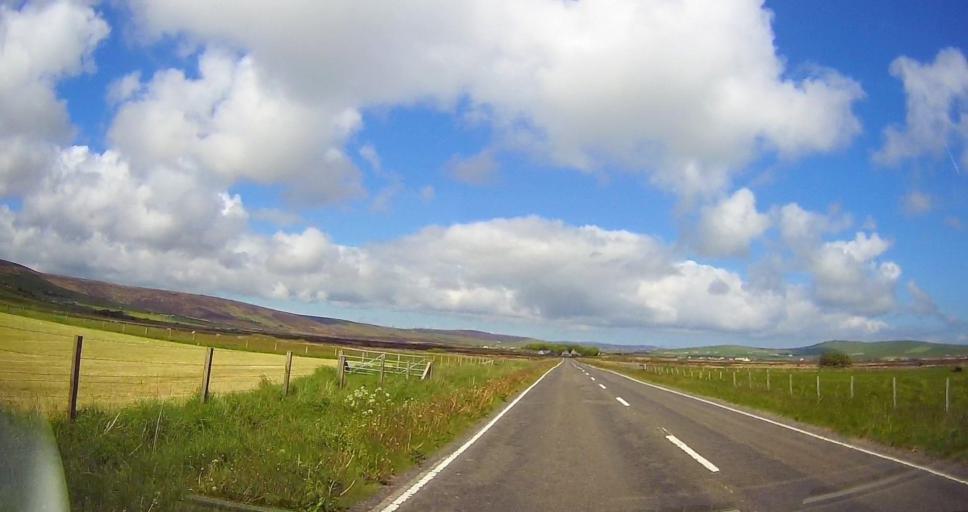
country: GB
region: Scotland
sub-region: Orkney Islands
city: Orkney
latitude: 59.0390
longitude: -3.0875
